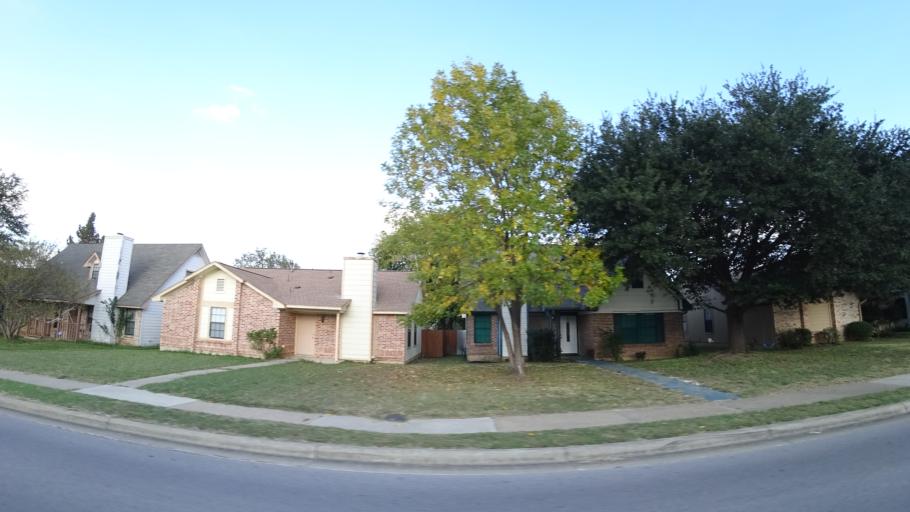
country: US
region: Texas
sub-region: Williamson County
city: Round Rock
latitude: 30.4924
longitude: -97.6639
